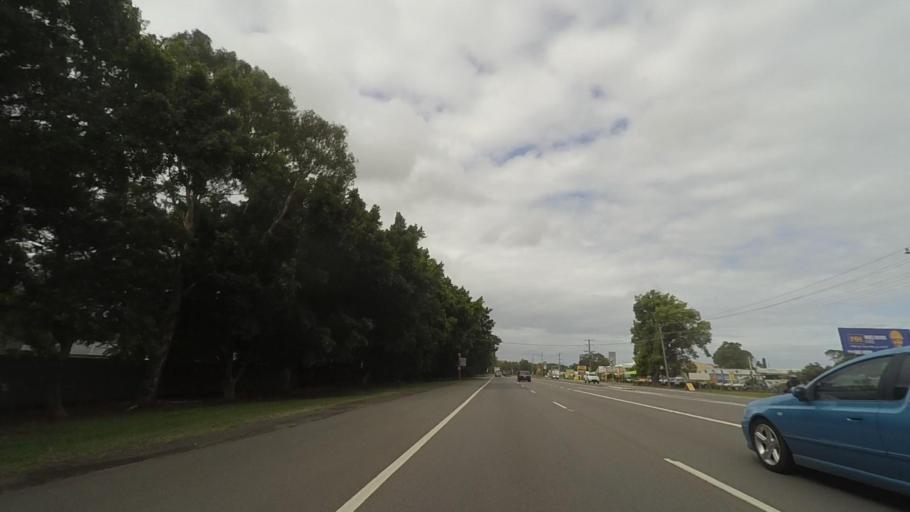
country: AU
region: New South Wales
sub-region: Port Stephens Shire
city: Raymond Terrace
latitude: -32.7853
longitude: 151.7324
